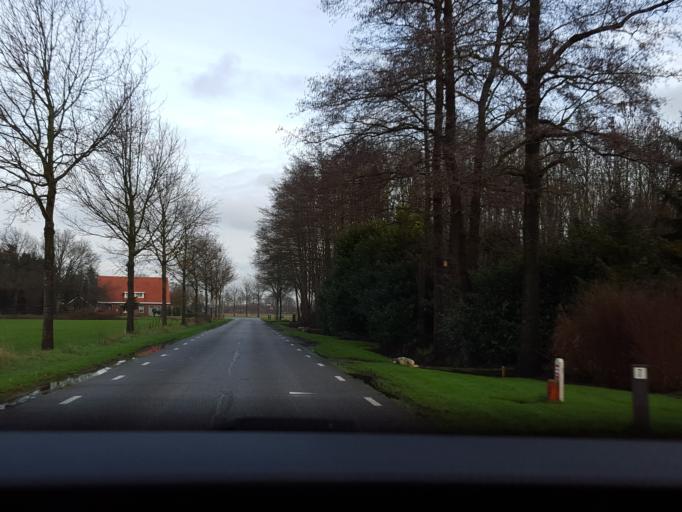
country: NL
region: Gelderland
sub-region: Oost Gelre
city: Lichtenvoorde
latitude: 52.0197
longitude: 6.5041
